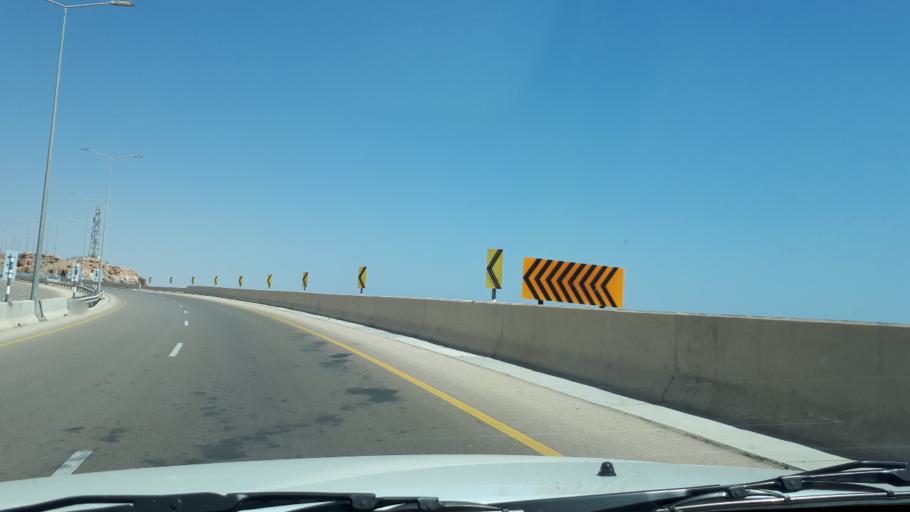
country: OM
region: Ash Sharqiyah
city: Sur
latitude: 22.8207
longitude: 59.2614
